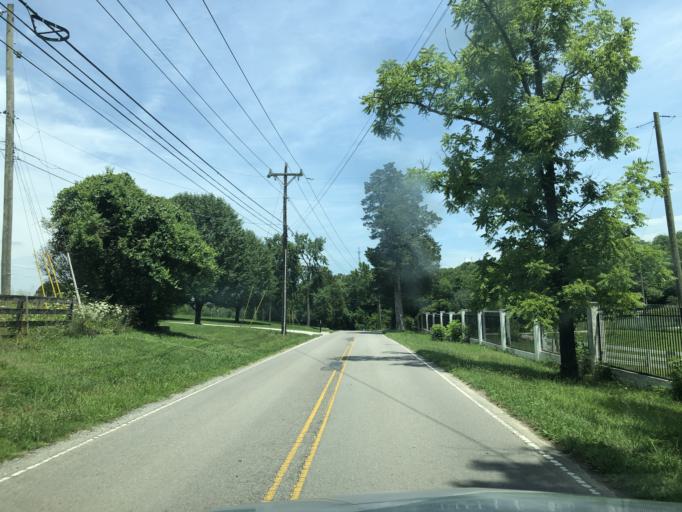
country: US
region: Tennessee
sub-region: Rutherford County
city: La Vergne
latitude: 36.0101
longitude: -86.6399
